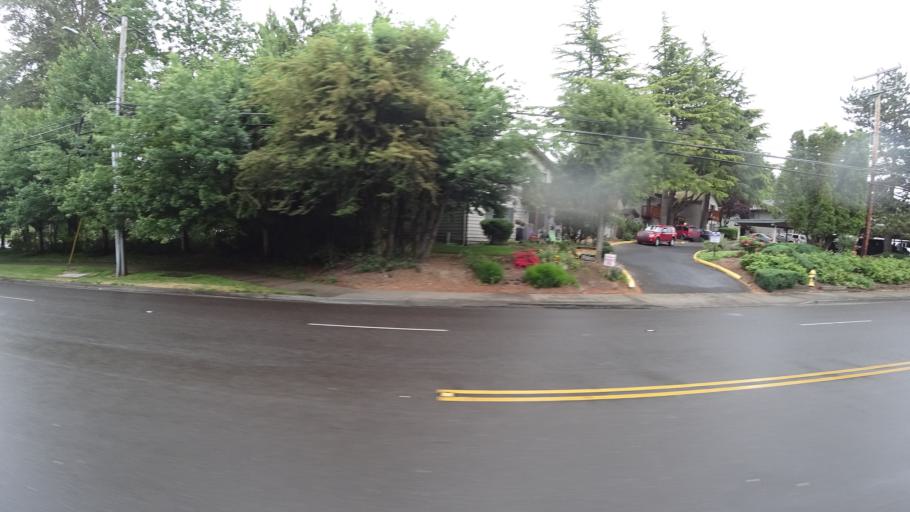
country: US
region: Oregon
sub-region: Washington County
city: Raleigh Hills
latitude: 45.4727
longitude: -122.7757
